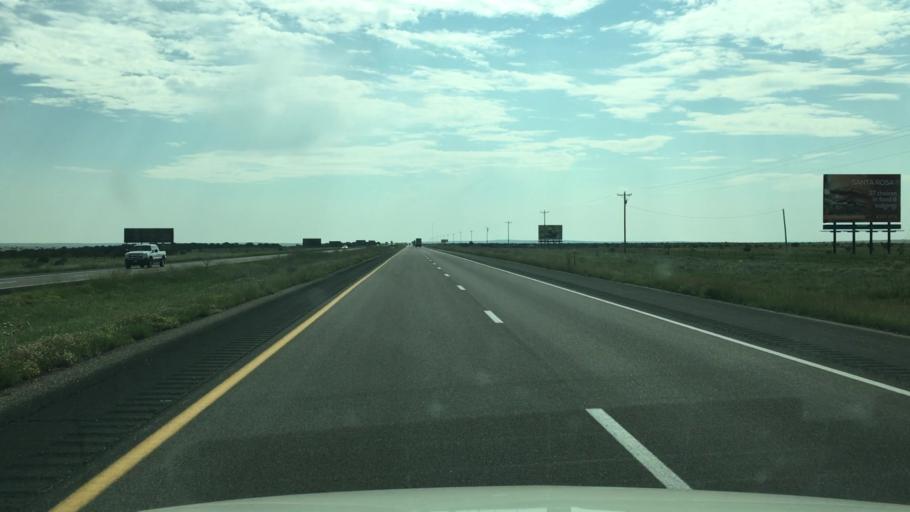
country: US
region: New Mexico
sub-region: San Miguel County
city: Las Vegas
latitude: 34.9938
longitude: -105.3430
